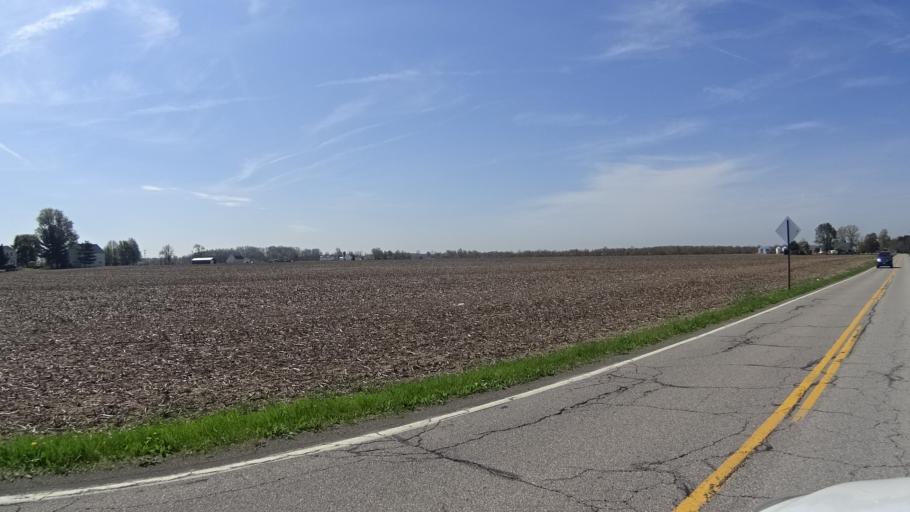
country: US
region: Ohio
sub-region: Lorain County
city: Elyria
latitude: 41.3124
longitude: -82.1204
